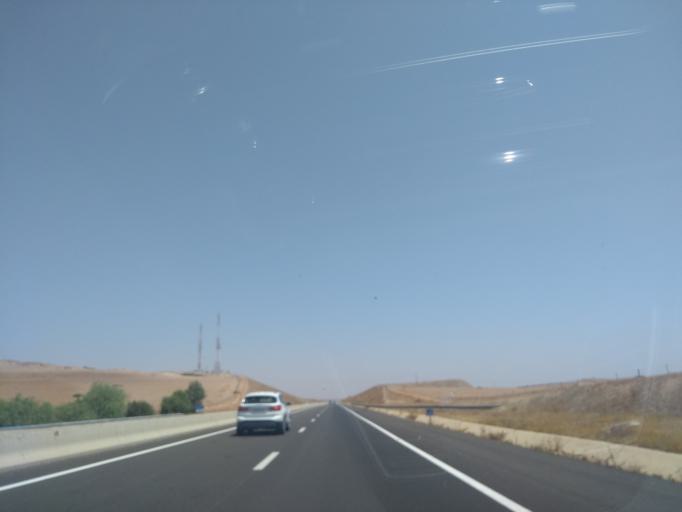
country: MA
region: Marrakech-Tensift-Al Haouz
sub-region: Kelaa-Des-Sraghna
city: Sidi Abdallah
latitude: 32.3062
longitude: -7.9590
